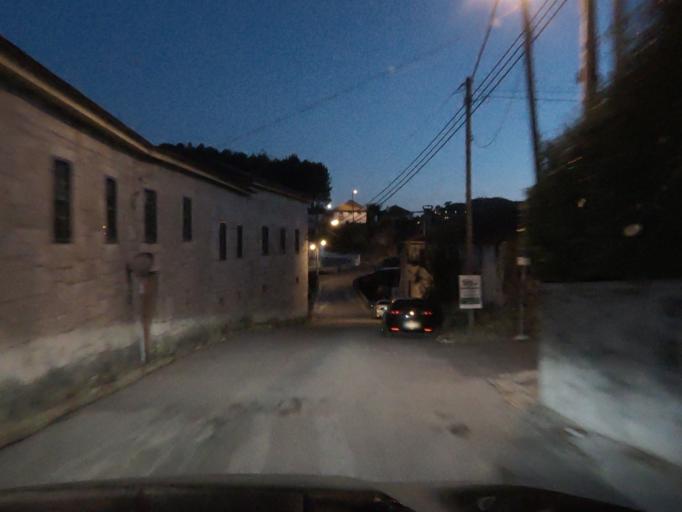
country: PT
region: Vila Real
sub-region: Vila Real
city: Vila Real
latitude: 41.3046
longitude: -7.7553
